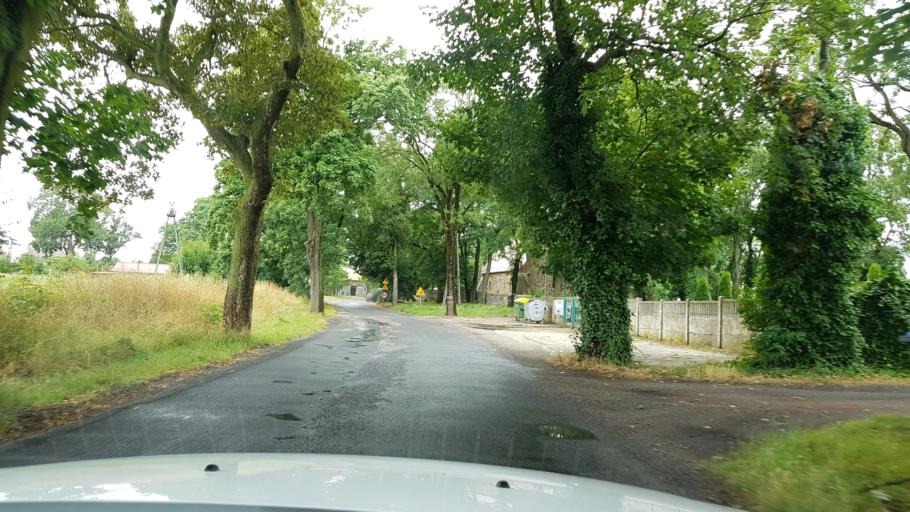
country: PL
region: West Pomeranian Voivodeship
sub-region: Powiat pyrzycki
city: Przelewice
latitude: 53.1076
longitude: 15.1285
